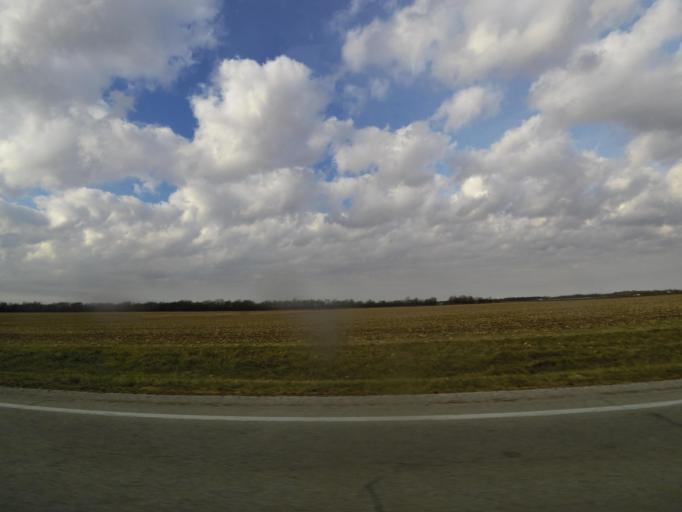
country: US
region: Illinois
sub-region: Fayette County
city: Ramsey
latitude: 39.2290
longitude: -89.1007
